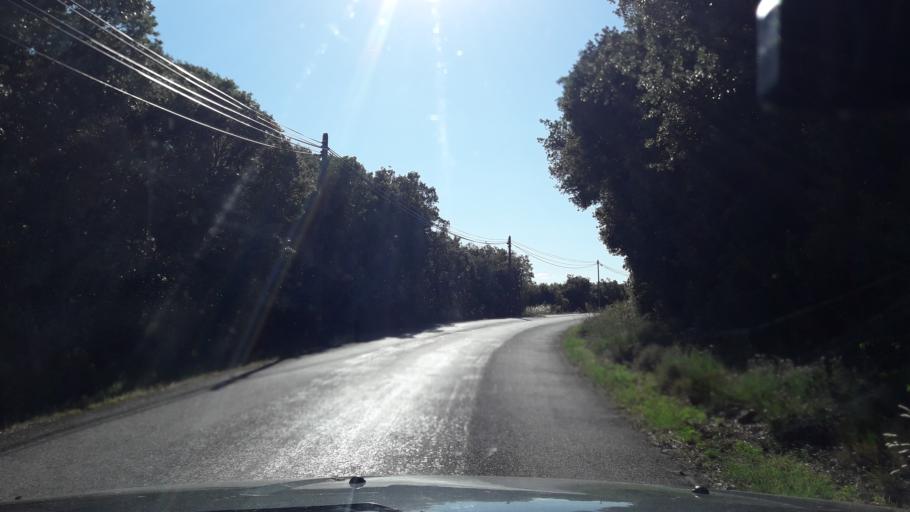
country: FR
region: Languedoc-Roussillon
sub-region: Departement du Gard
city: Saint-Julien-de-Peyrolas
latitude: 44.3719
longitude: 4.5103
